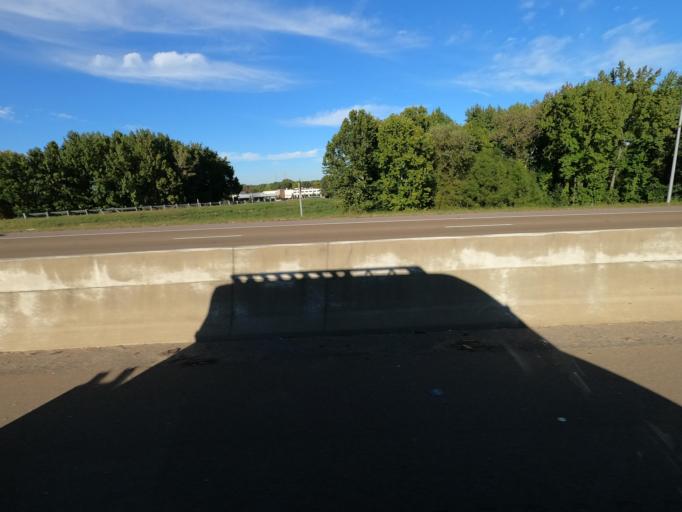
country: US
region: Tennessee
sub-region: Shelby County
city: Germantown
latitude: 35.0739
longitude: -89.8600
